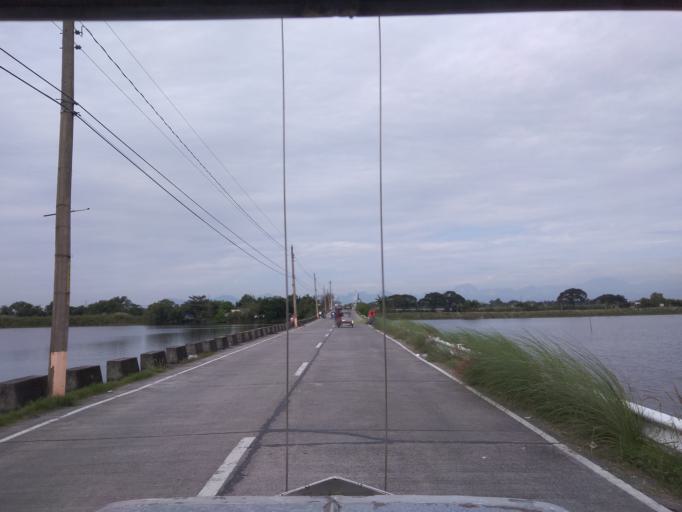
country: PH
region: Central Luzon
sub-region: Province of Pampanga
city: Lubao
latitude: 14.9379
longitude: 120.6112
